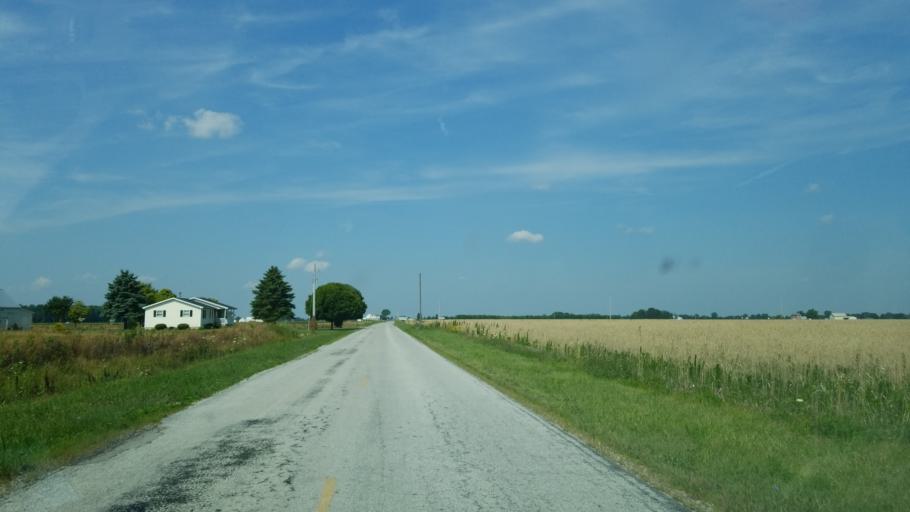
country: US
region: Ohio
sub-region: Seneca County
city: Tiffin
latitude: 41.1665
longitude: -83.2725
